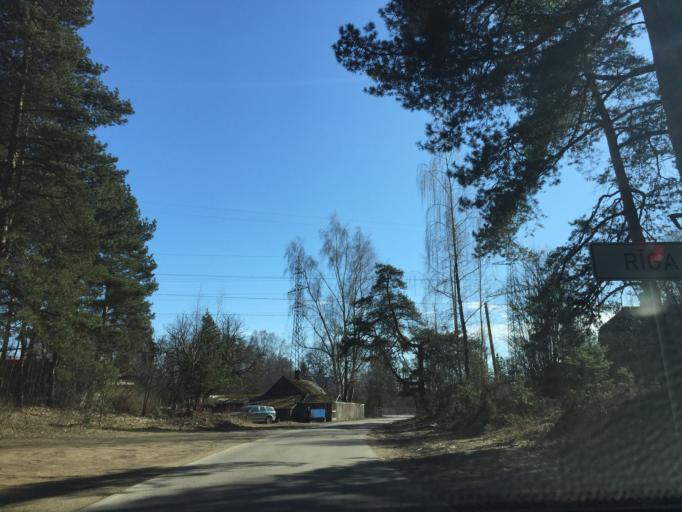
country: LV
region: Marupe
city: Marupe
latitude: 56.9639
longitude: 23.9963
